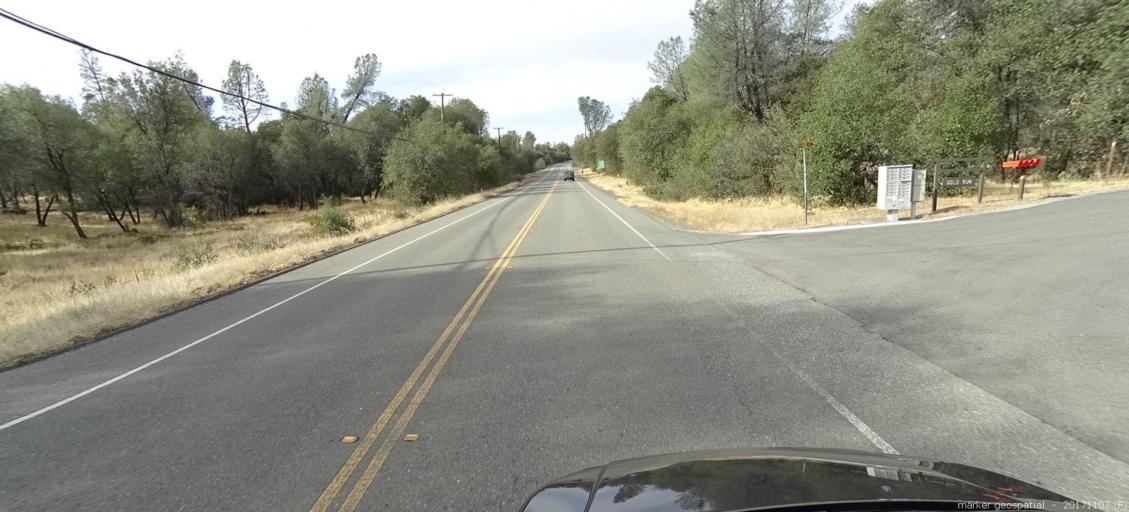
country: US
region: California
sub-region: Shasta County
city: Shasta
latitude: 40.5185
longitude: -122.4831
